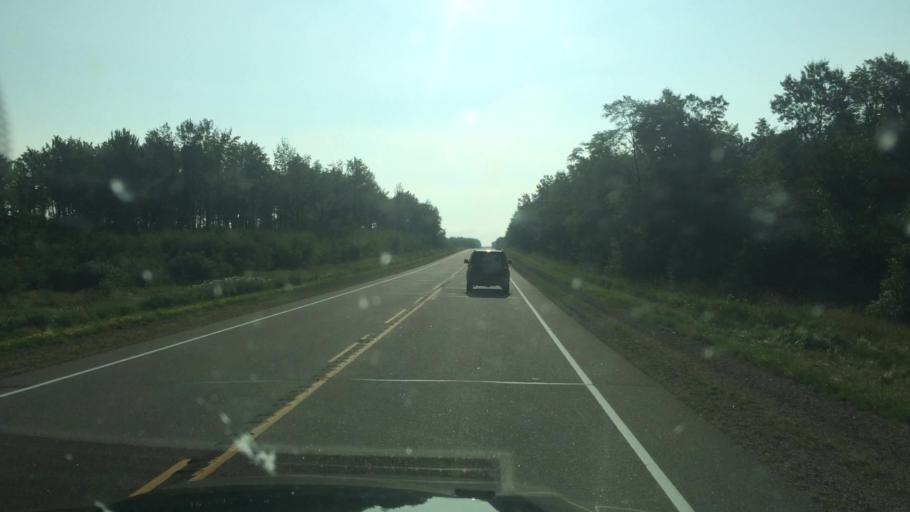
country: US
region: Wisconsin
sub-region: Langlade County
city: Antigo
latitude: 45.1469
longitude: -89.3792
